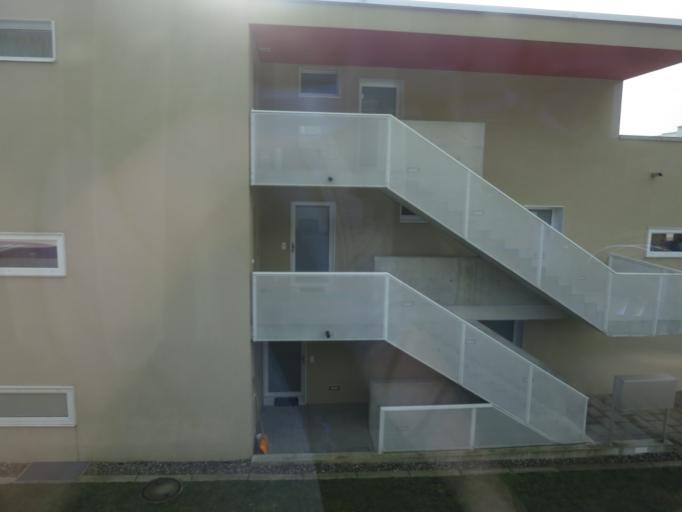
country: CH
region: Zurich
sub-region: Bezirk Meilen
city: Dorf
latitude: 47.2358
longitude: 8.7452
